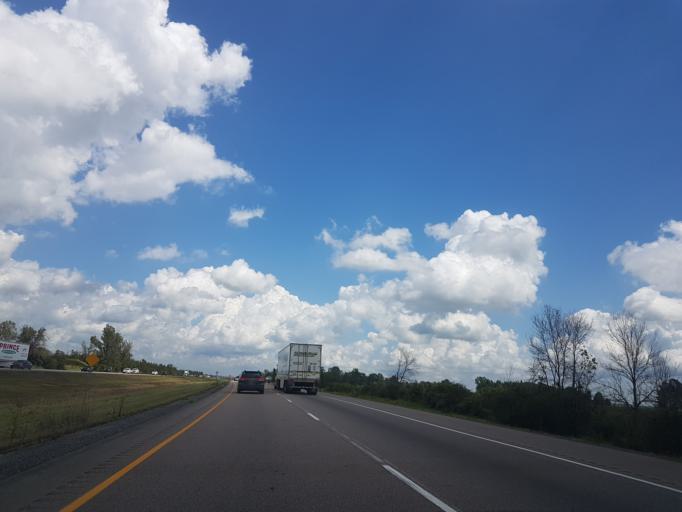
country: CA
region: Ontario
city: Napanee Downtown
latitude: 44.2543
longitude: -76.9942
